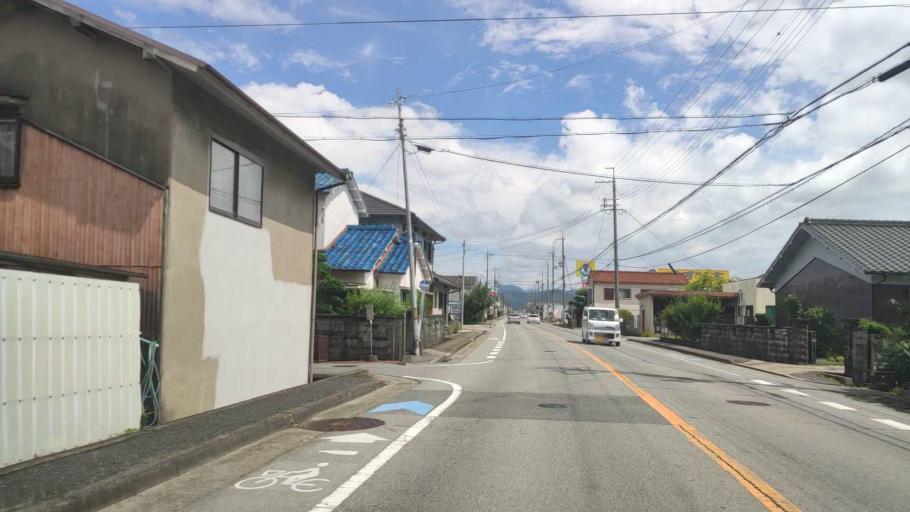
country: JP
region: Hyogo
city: Nishiwaki
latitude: 35.0019
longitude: 134.9627
